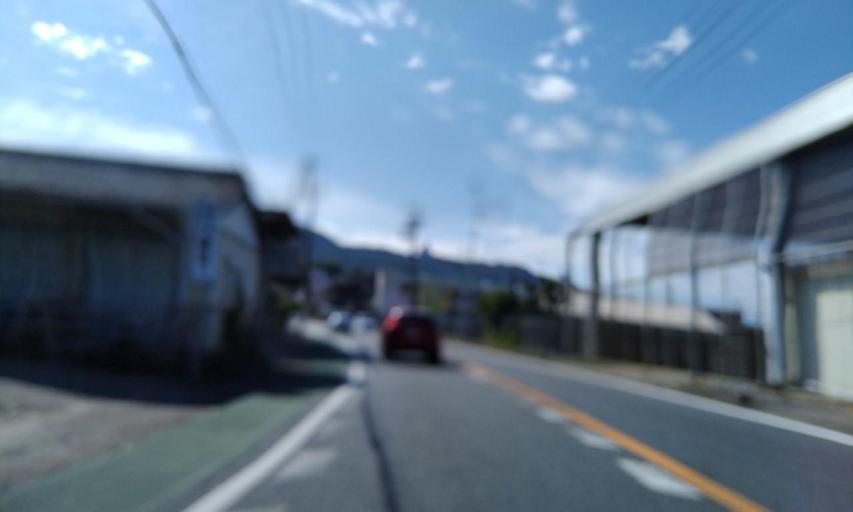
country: JP
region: Wakayama
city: Kainan
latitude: 34.0226
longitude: 135.1794
